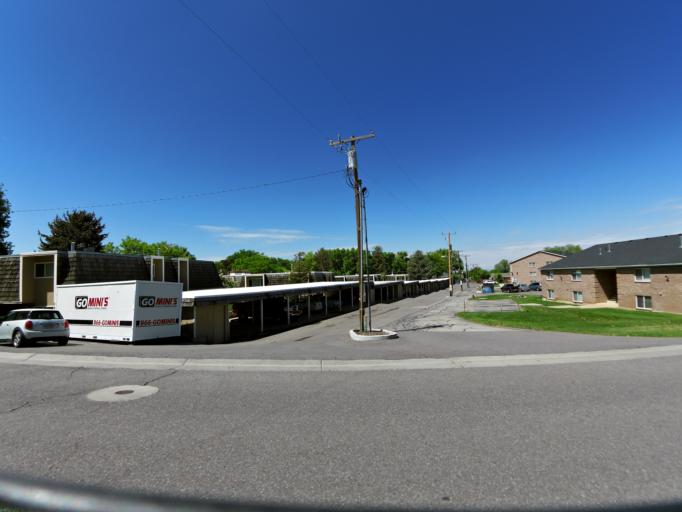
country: US
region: Utah
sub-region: Weber County
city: Washington Terrace
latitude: 41.1743
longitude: -111.9465
